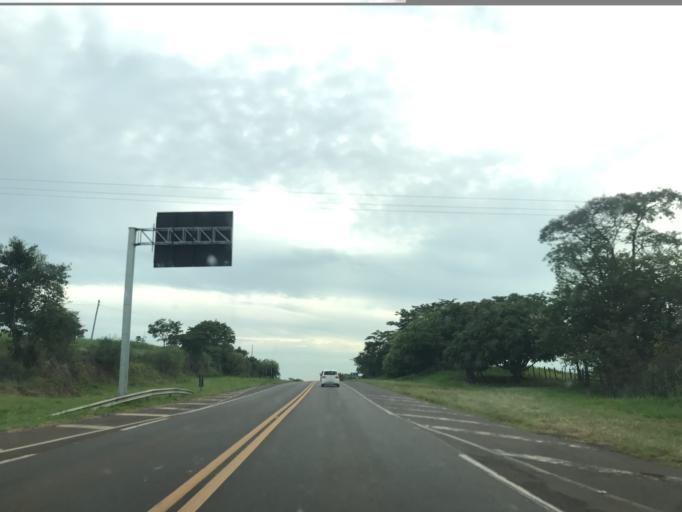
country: BR
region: Sao Paulo
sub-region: Birigui
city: Birigui
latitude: -21.5692
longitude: -50.4351
